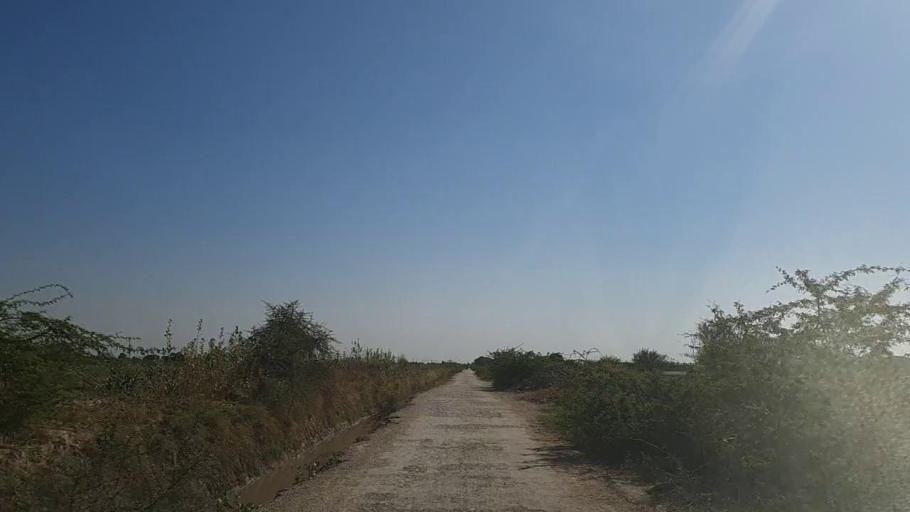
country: PK
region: Sindh
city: Samaro
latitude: 25.2440
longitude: 69.4836
